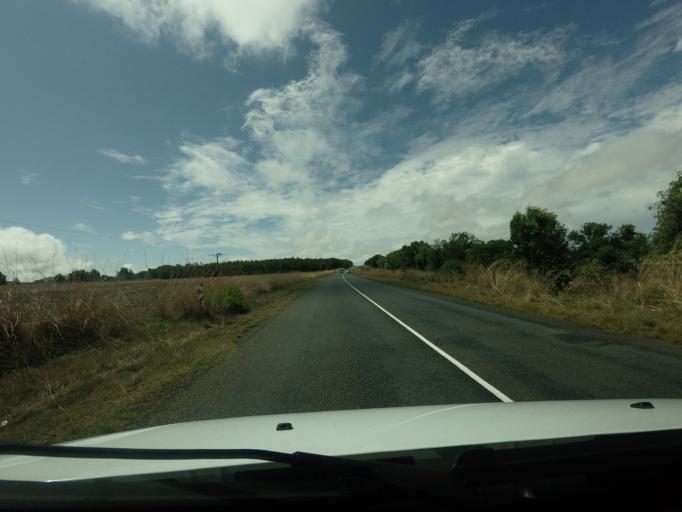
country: ZA
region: Mpumalanga
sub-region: Ehlanzeni District
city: Lydenburg
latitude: -25.1897
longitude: 30.3588
